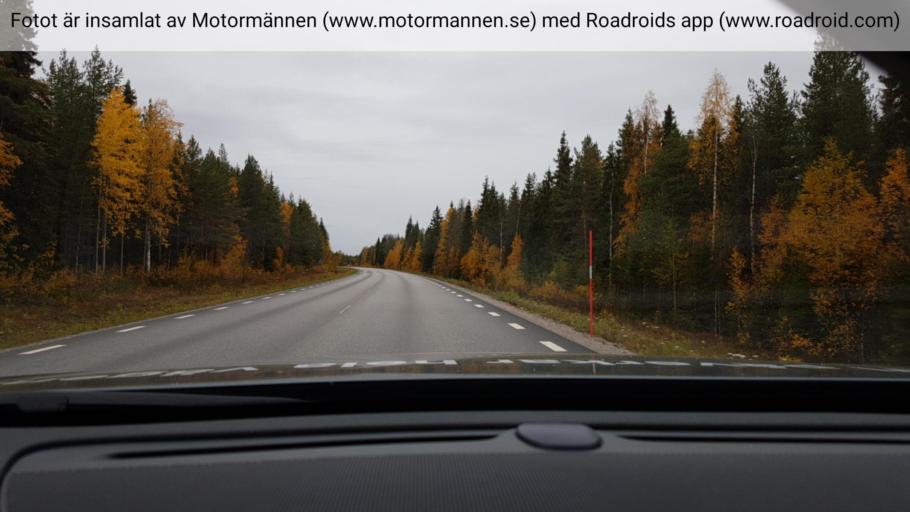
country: SE
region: Norrbotten
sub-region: Overkalix Kommun
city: OEverkalix
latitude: 66.3444
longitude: 22.8297
